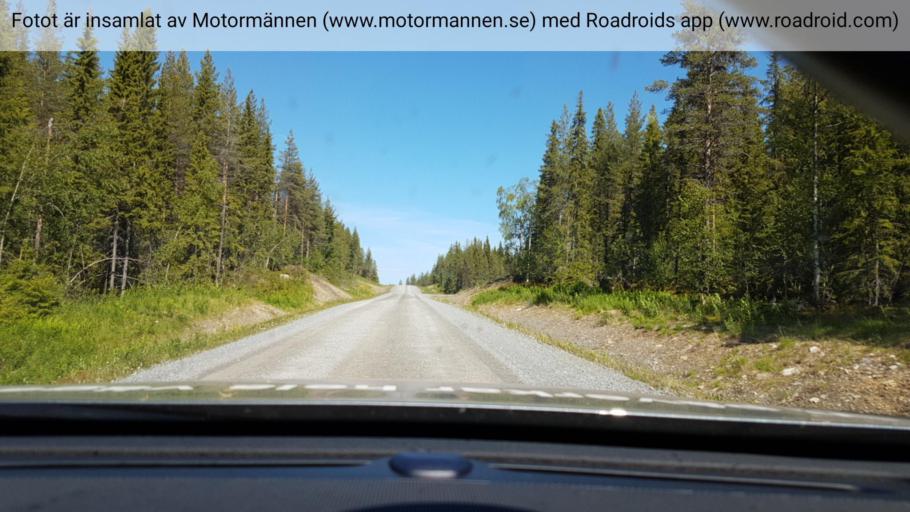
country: SE
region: Vaesterbotten
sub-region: Vilhelmina Kommun
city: Sjoberg
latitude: 64.6694
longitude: 15.7573
